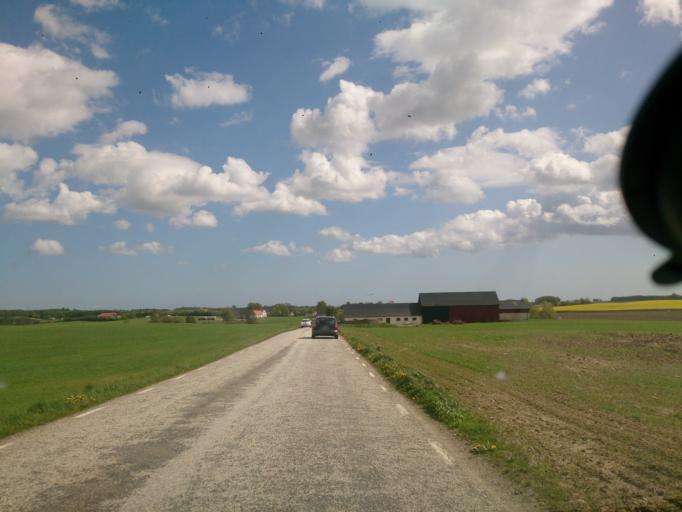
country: SE
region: Skane
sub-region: Skurups Kommun
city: Rydsgard
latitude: 55.4936
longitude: 13.7076
